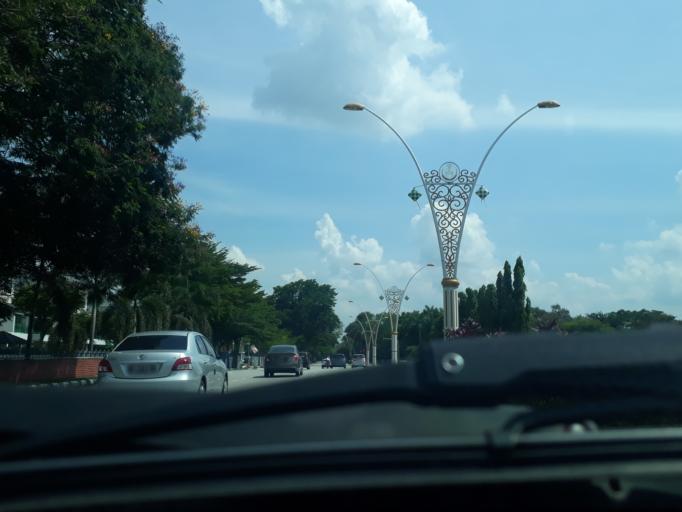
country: MY
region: Perak
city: Ipoh
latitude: 4.5936
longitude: 101.1184
